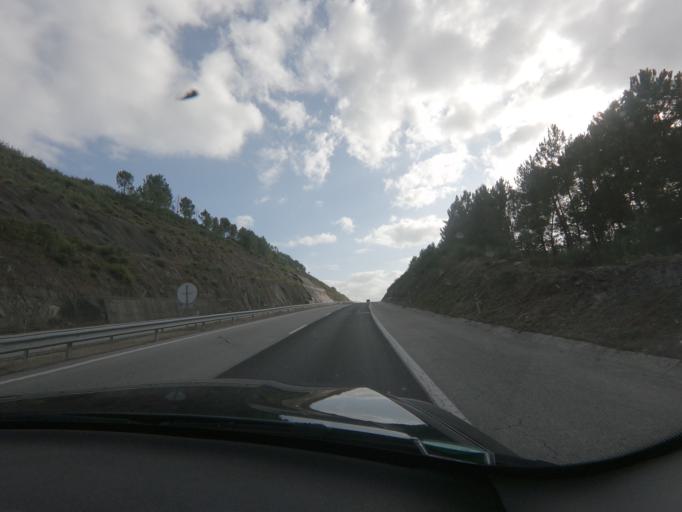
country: PT
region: Viseu
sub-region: Castro Daire
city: Castro Daire
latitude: 40.8399
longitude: -7.9292
